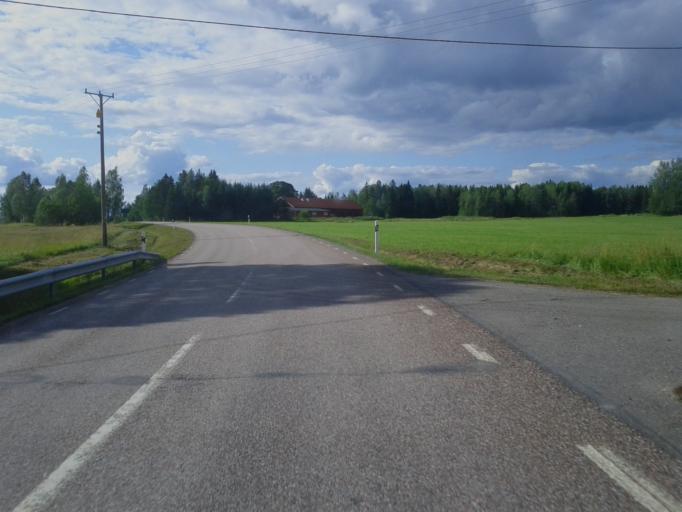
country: SE
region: Vaestmanland
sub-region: Sala Kommun
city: Sala
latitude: 59.9144
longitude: 16.5182
